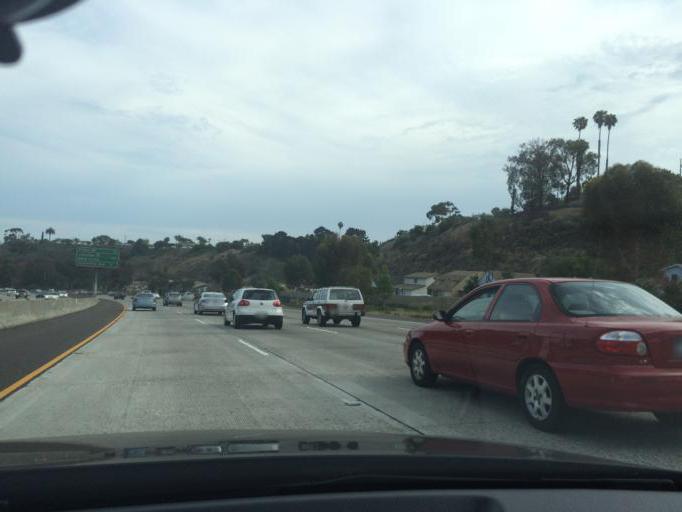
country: US
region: California
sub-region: San Diego County
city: San Diego
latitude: 32.7809
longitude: -117.1630
